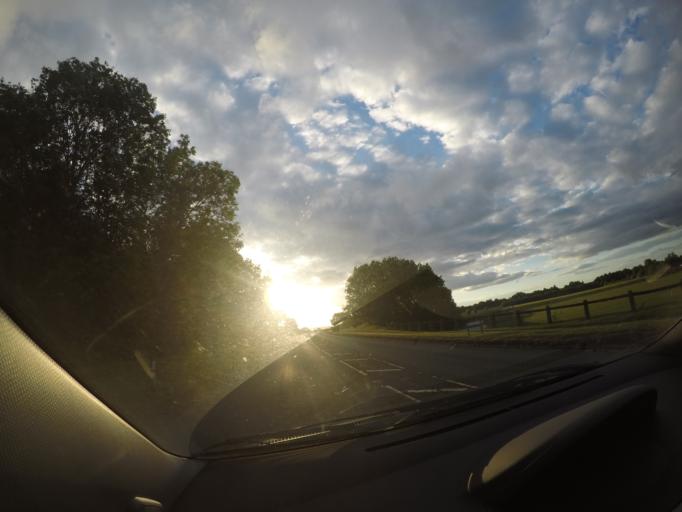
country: GB
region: England
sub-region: North Yorkshire
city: Catterick
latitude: 54.3800
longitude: -1.6369
